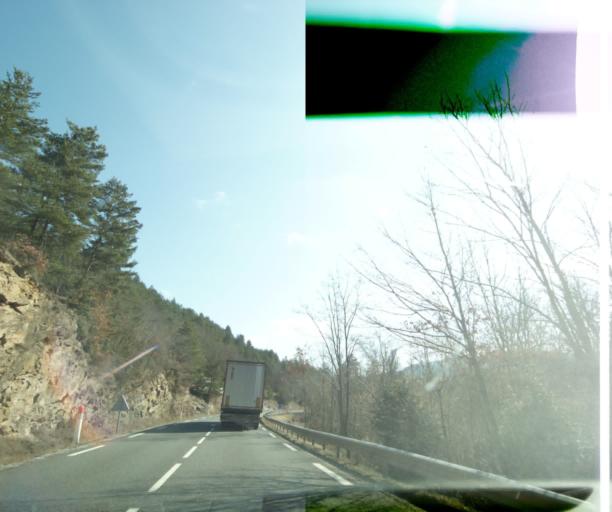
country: FR
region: Languedoc-Roussillon
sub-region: Departement de la Lozere
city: Chirac
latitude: 44.4919
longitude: 3.2650
